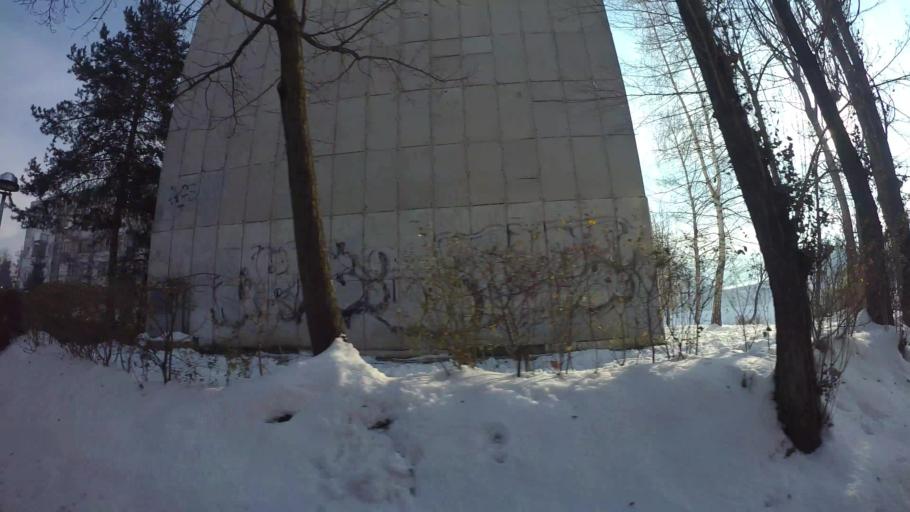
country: BA
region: Federation of Bosnia and Herzegovina
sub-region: Kanton Sarajevo
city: Sarajevo
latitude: 43.8461
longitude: 18.3683
